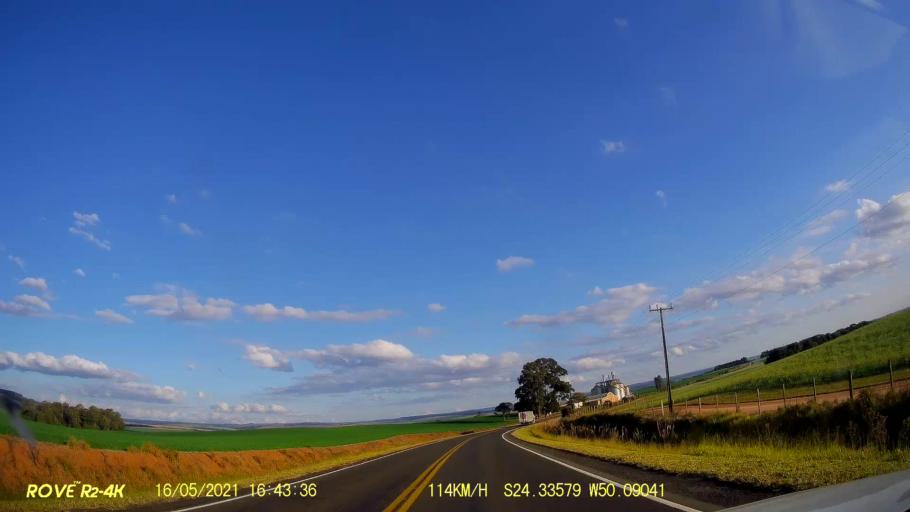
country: BR
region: Parana
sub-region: Pirai Do Sul
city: Pirai do Sul
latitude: -24.3360
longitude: -50.0904
